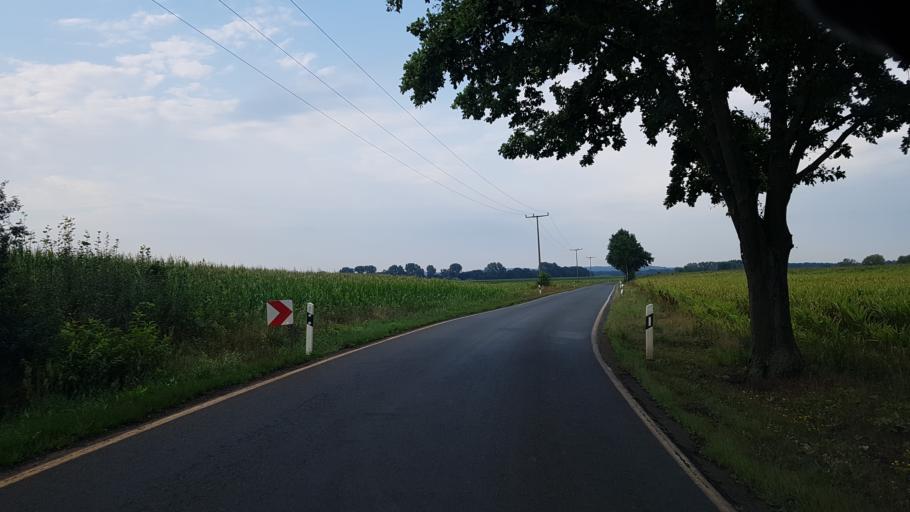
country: DE
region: Brandenburg
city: Tettau
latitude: 51.4210
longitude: 13.7290
